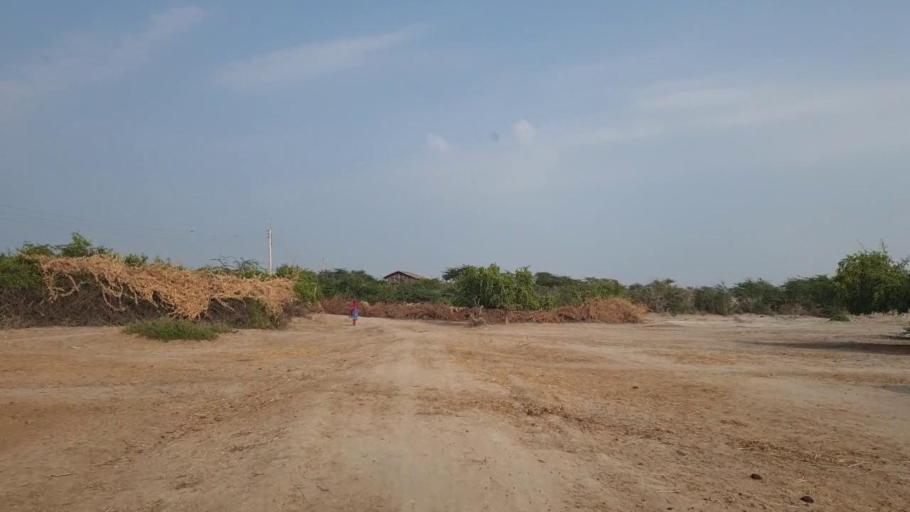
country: PK
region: Sindh
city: Kadhan
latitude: 24.4563
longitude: 68.8138
